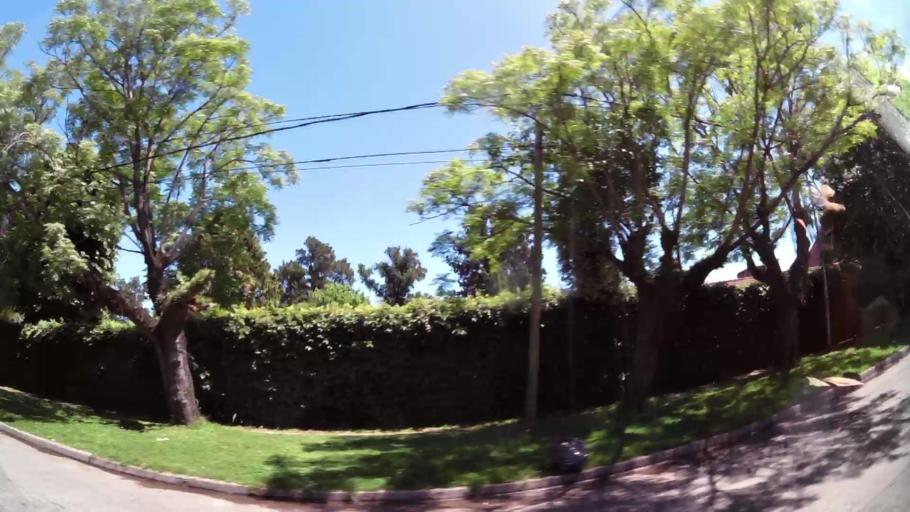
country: AR
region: Buenos Aires
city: Hurlingham
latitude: -34.4978
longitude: -58.6431
